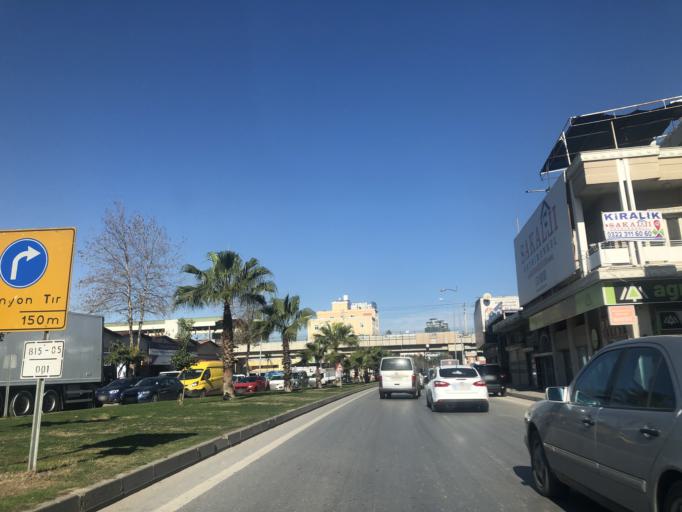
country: TR
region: Adana
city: Yuregir
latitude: 36.9801
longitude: 35.3387
